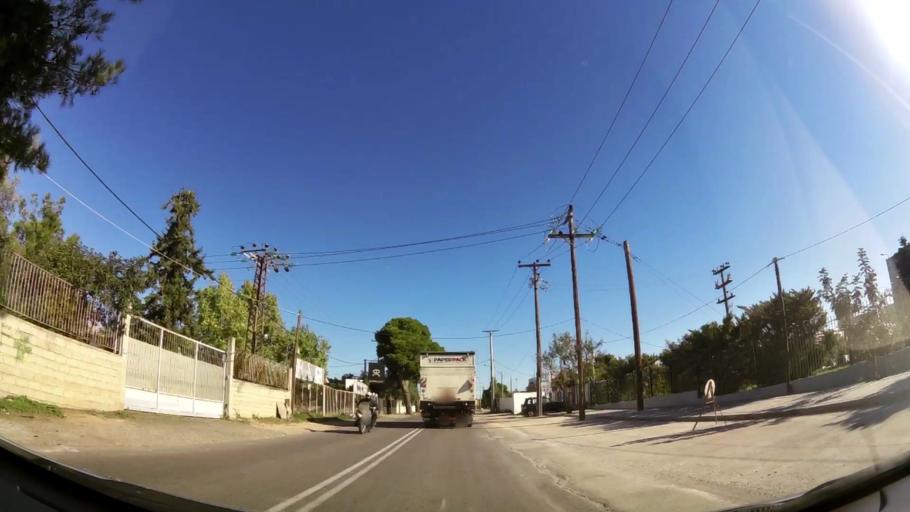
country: GR
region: Attica
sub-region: Nomarchia Athinas
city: Lykovrysi
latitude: 38.0935
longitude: 23.7751
